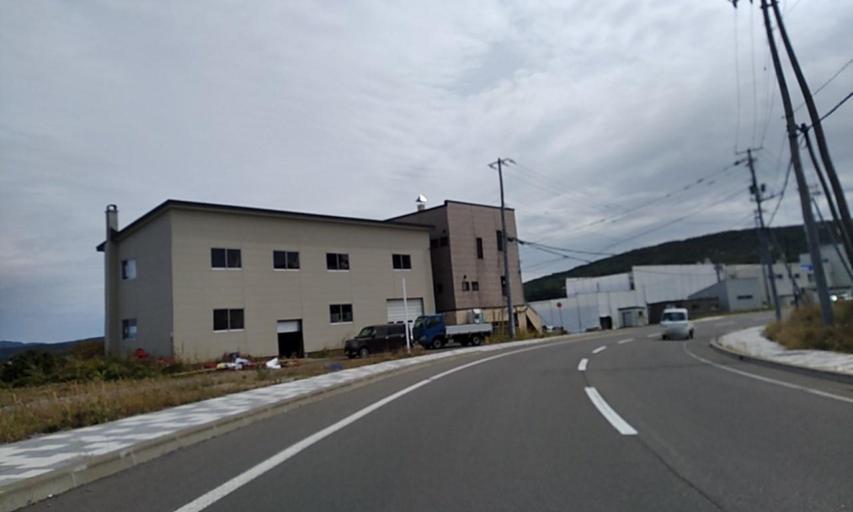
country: JP
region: Hokkaido
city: Rumoi
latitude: 43.8575
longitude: 141.5278
